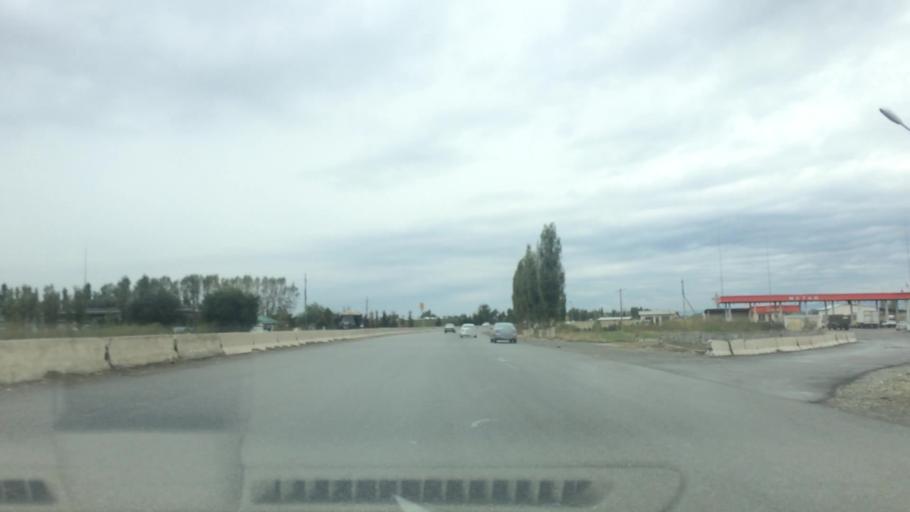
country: UZ
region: Jizzax
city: Jizzax
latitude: 40.0231
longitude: 67.6151
